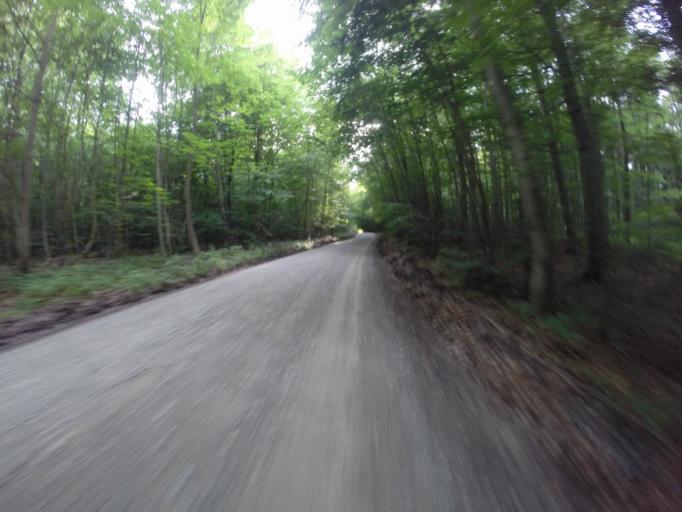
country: DE
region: Thuringia
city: Grosslobichau
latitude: 50.9116
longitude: 11.6483
